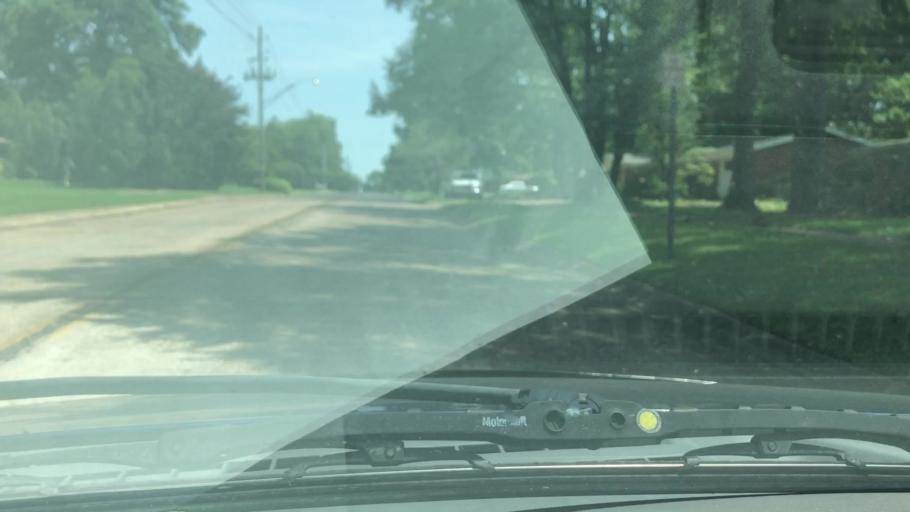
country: US
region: Arkansas
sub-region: Miller County
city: Texarkana
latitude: 33.4557
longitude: -94.0601
